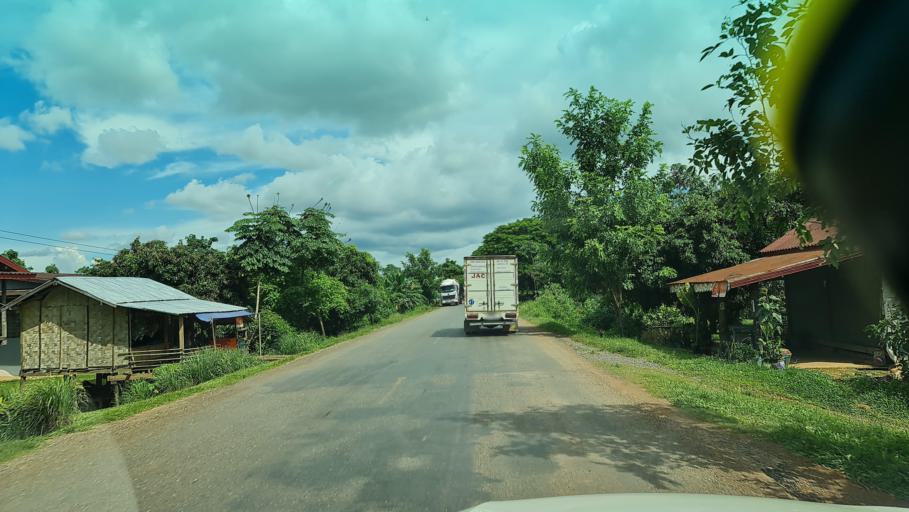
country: LA
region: Bolikhamxai
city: Ban Nahin
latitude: 18.1920
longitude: 104.2215
